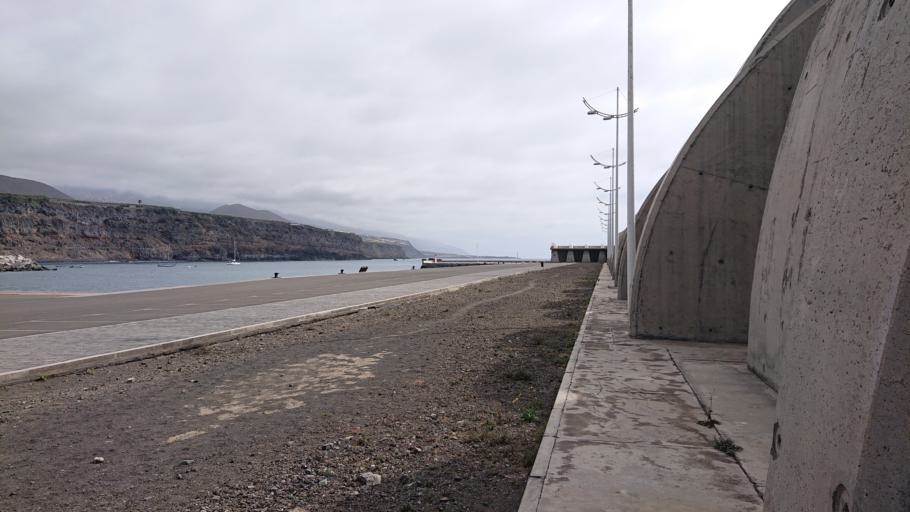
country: ES
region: Canary Islands
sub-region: Provincia de Santa Cruz de Tenerife
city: Tazacorte
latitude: 28.6431
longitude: -17.9443
